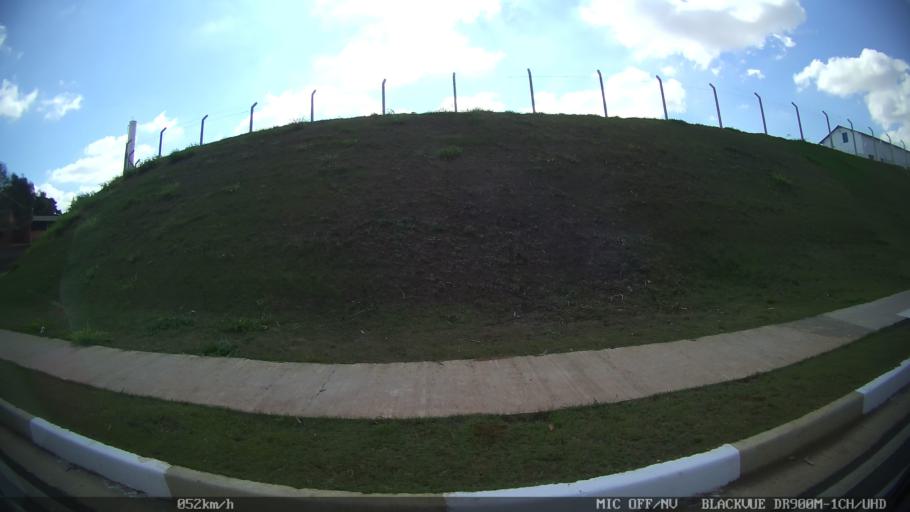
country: BR
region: Sao Paulo
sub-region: Hortolandia
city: Hortolandia
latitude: -22.8886
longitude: -47.2061
